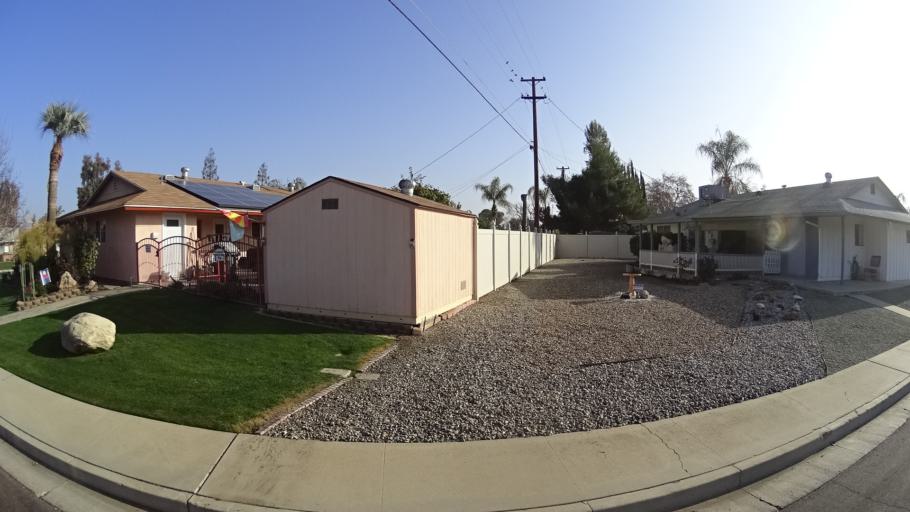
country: US
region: California
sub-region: Kern County
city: Greenacres
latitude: 35.3510
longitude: -119.0686
